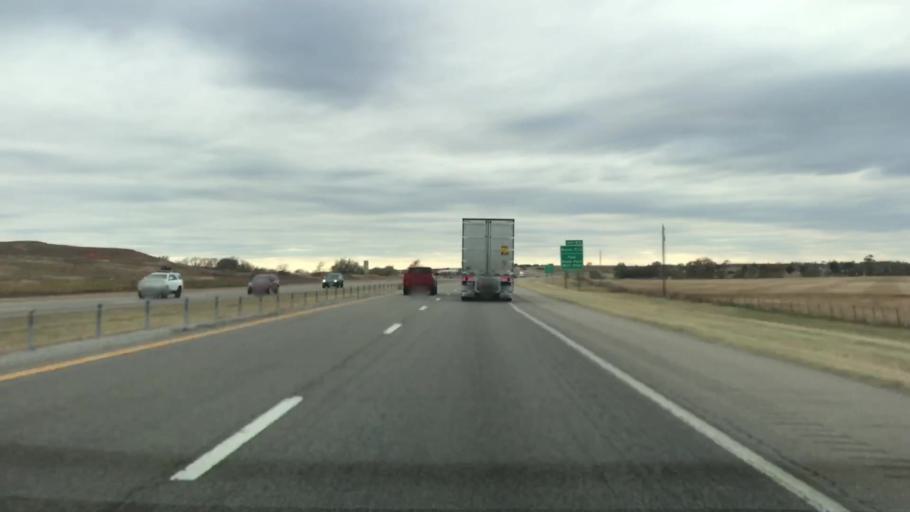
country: US
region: Oklahoma
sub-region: Washita County
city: Burns Flat
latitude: 35.4502
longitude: -99.1602
